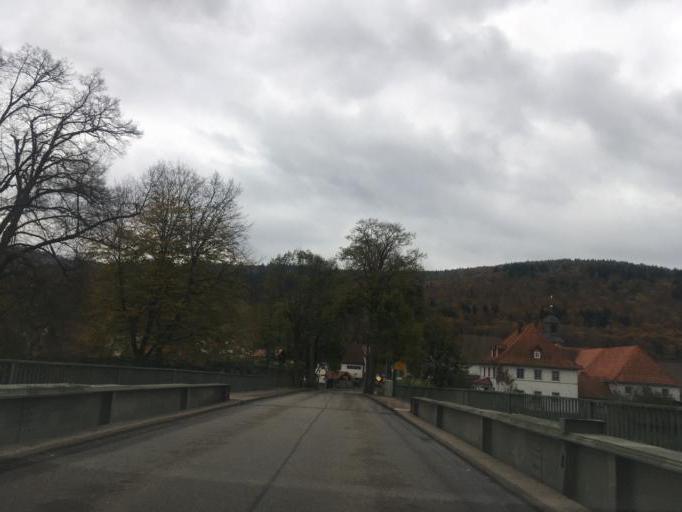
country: DE
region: Lower Saxony
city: Bodenfelde
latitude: 51.6009
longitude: 9.5514
